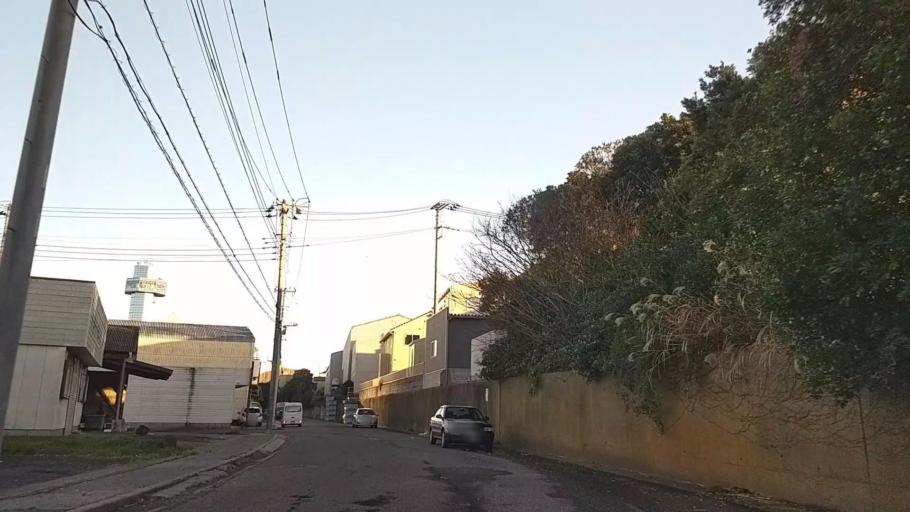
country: JP
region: Chiba
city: Hasaki
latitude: 35.7417
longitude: 140.8590
